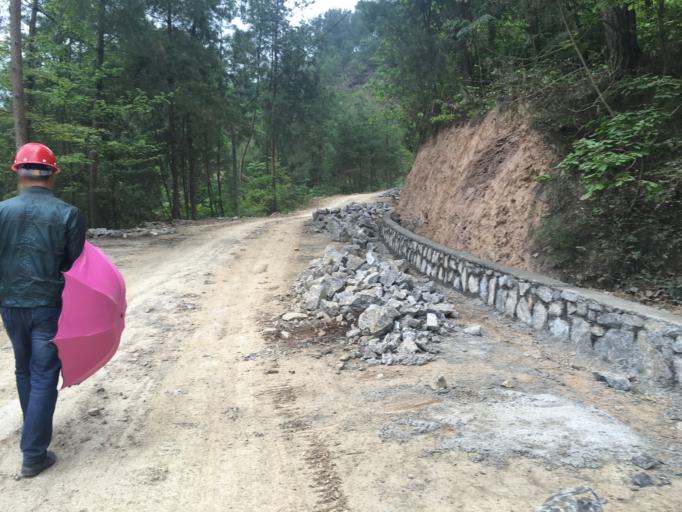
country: CN
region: Guizhou Sheng
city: Changbao
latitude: 28.2081
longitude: 108.2844
